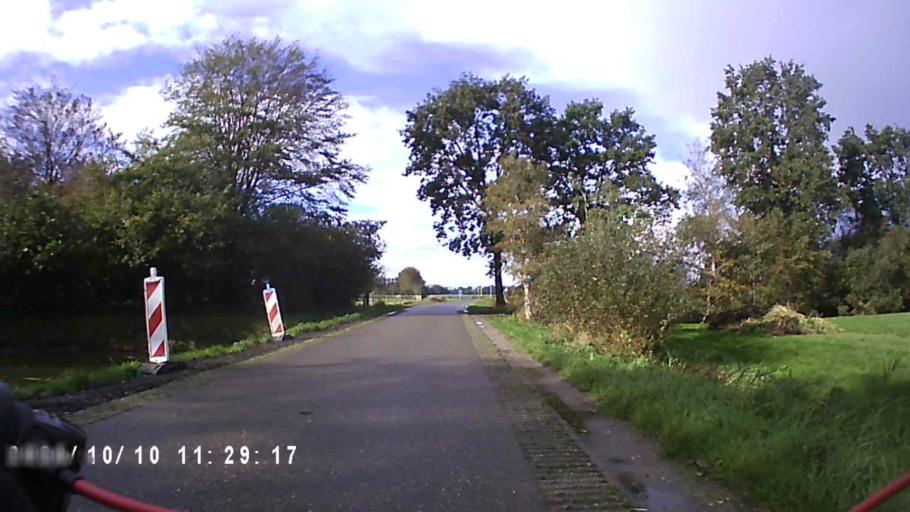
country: NL
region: Friesland
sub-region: Gemeente Smallingerland
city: Drachtstercompagnie
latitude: 53.0865
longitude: 6.1487
